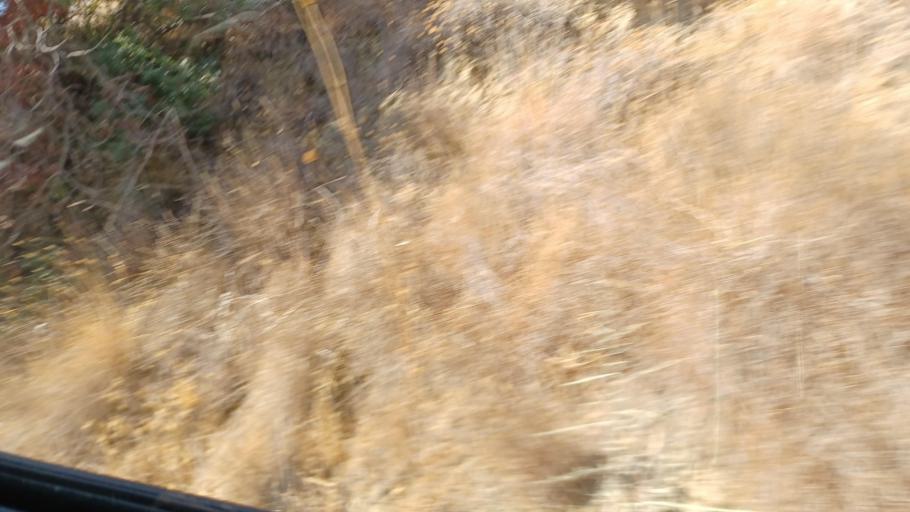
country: CY
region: Pafos
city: Polis
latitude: 34.9640
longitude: 32.4664
